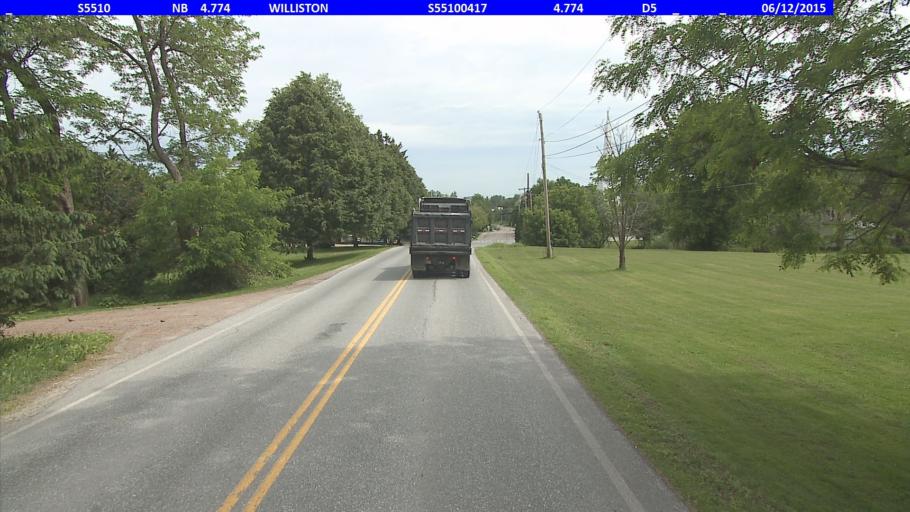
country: US
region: Vermont
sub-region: Chittenden County
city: Williston
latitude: 44.4366
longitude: -73.0691
